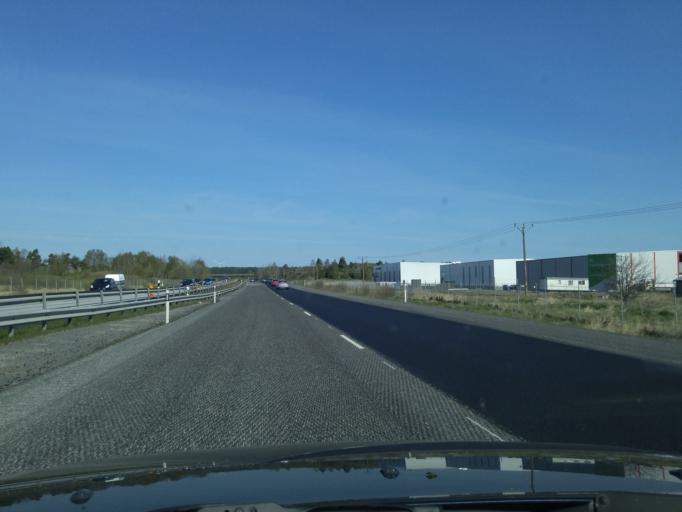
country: SE
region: Vaestra Goetaland
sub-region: Kungalvs Kommun
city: Kungalv
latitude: 57.8947
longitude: 11.9309
